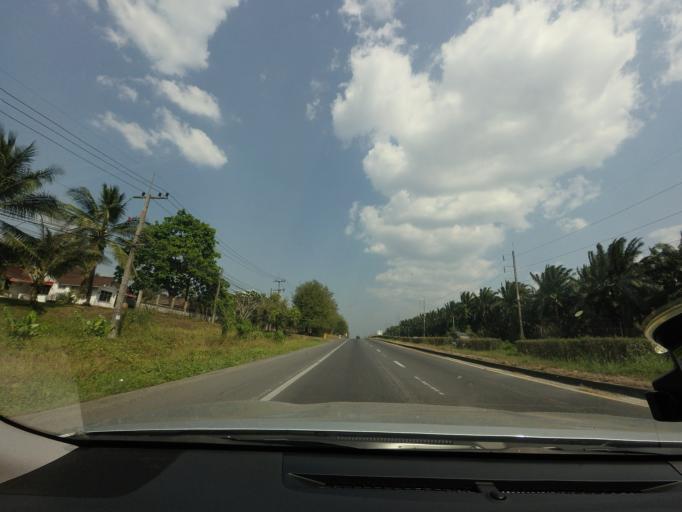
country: TH
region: Phangnga
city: Thap Put
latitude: 8.5092
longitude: 98.6505
